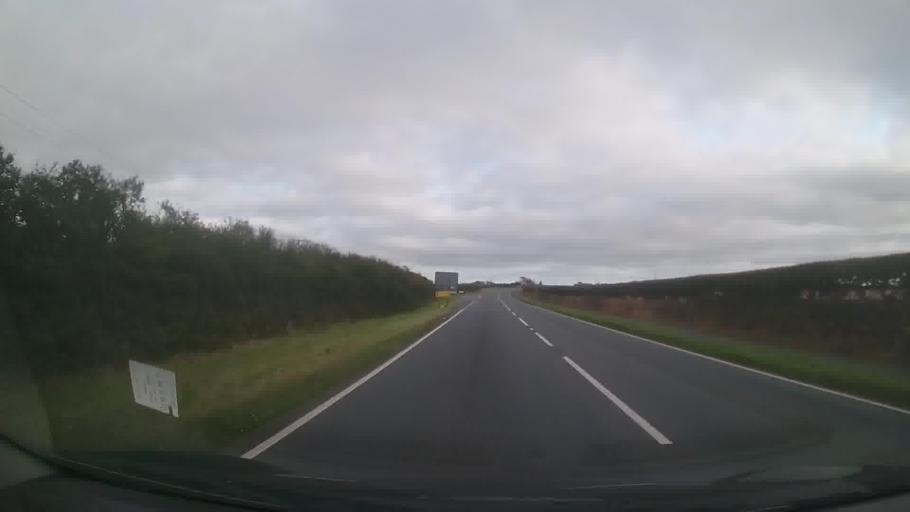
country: GB
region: Wales
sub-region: Pembrokeshire
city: Johnston
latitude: 51.7309
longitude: -4.9895
